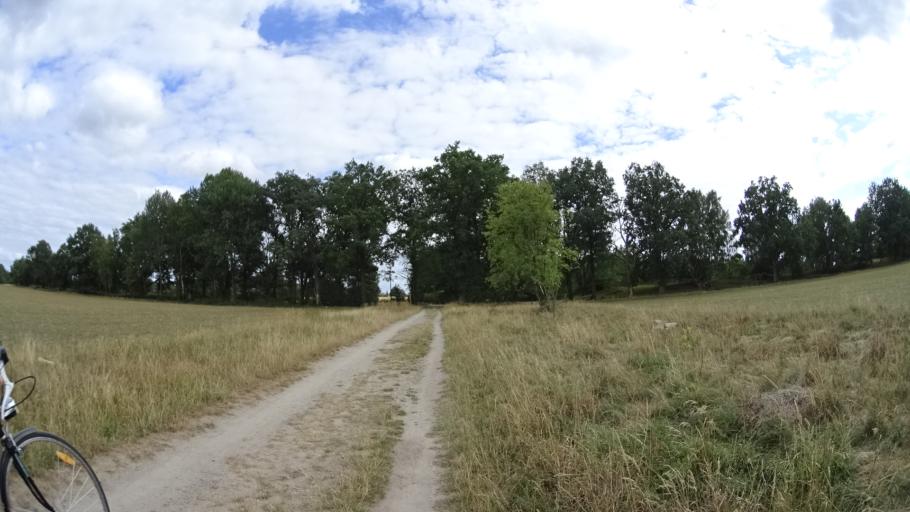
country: DE
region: Lower Saxony
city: Undeloh
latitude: 53.1620
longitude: 9.9614
